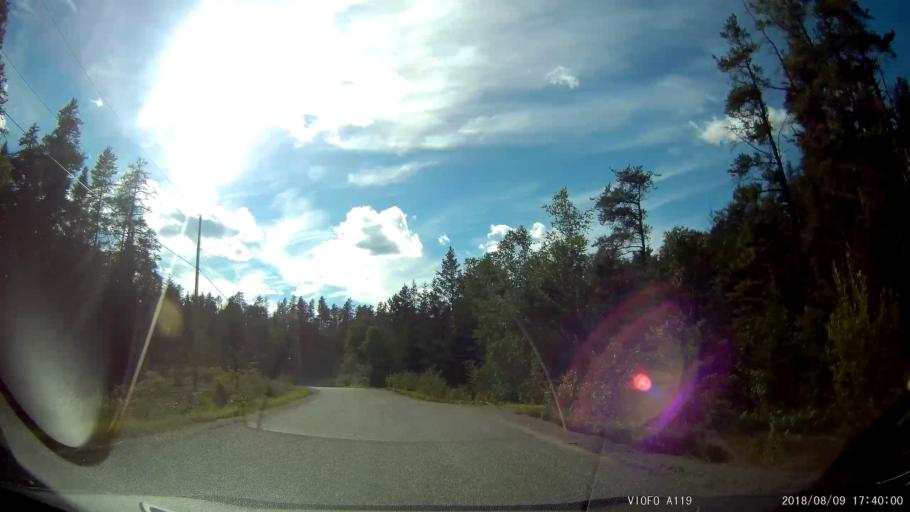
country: CA
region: Ontario
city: Rayside-Balfour
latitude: 46.6061
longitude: -81.4983
